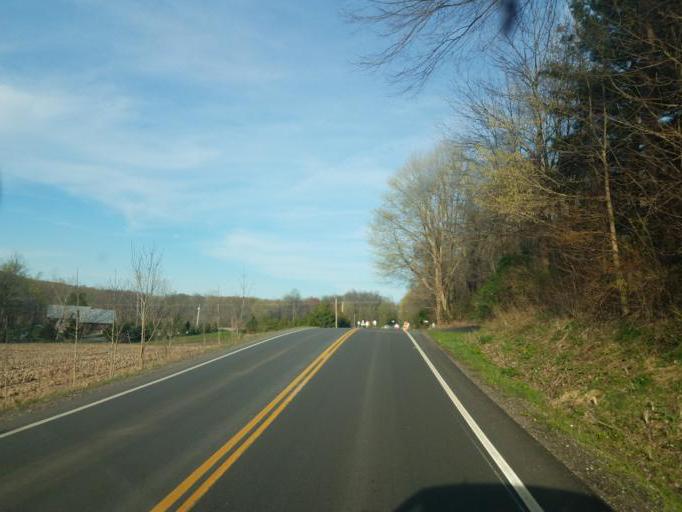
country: US
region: Ohio
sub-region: Richland County
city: Lexington
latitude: 40.7050
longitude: -82.6682
